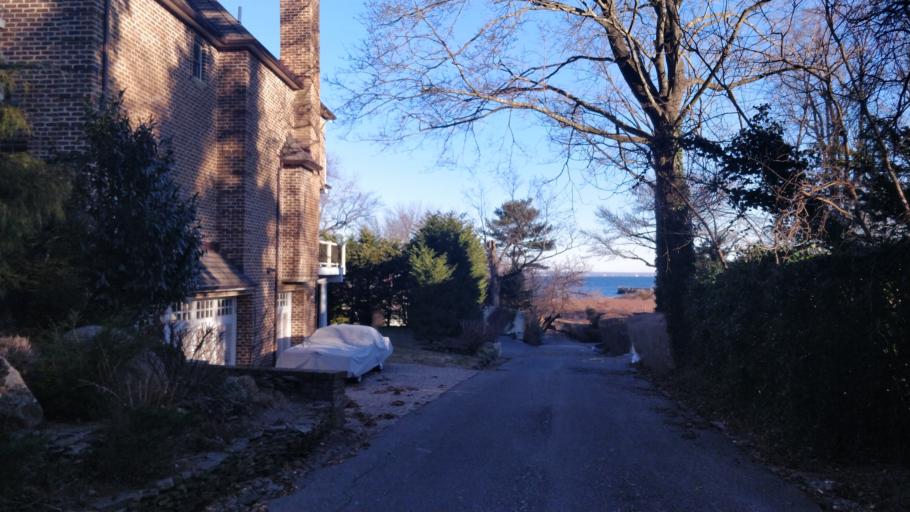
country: US
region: New York
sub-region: Nassau County
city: Glen Cove
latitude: 40.8797
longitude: -73.6487
